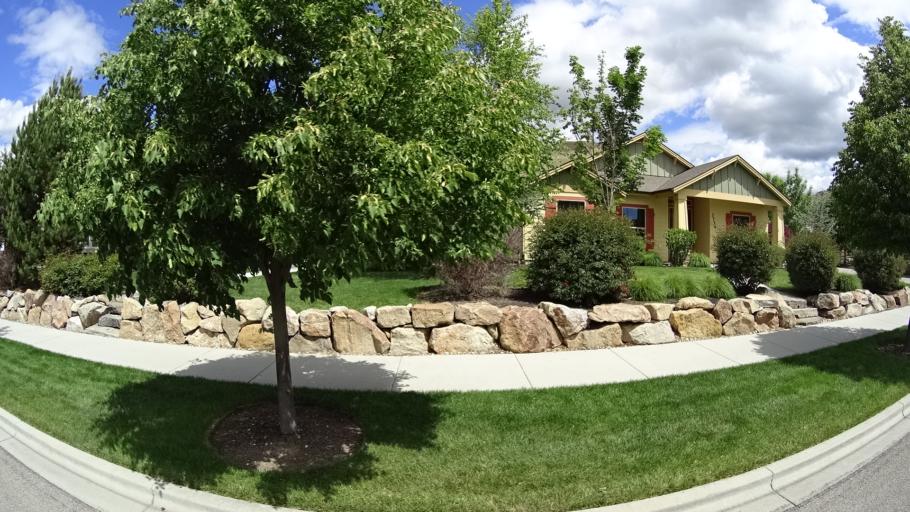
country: US
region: Idaho
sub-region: Ada County
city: Boise
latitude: 43.5780
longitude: -116.1378
